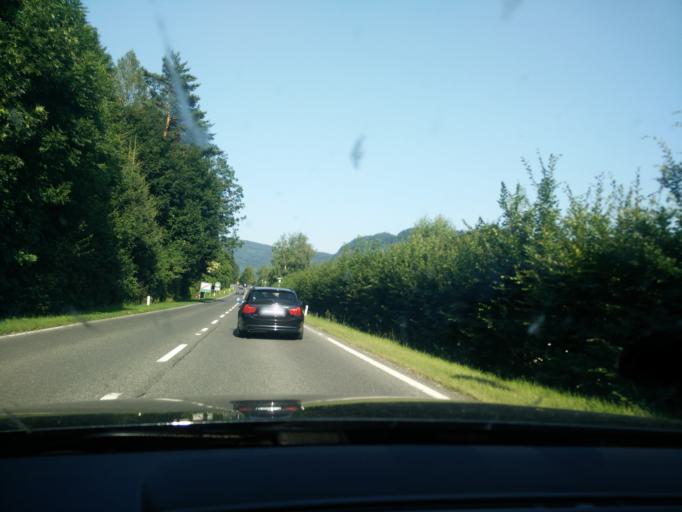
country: AT
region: Carinthia
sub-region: Politischer Bezirk Villach Land
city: Wernberg
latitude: 46.6634
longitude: 13.9179
